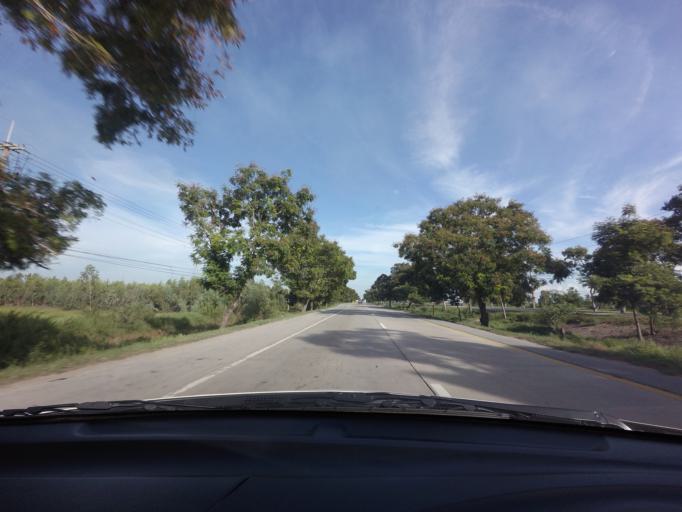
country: TH
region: Phra Nakhon Si Ayutthaya
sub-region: Amphoe Bang Sai
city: Bang Sai
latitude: 14.2715
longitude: 100.2500
